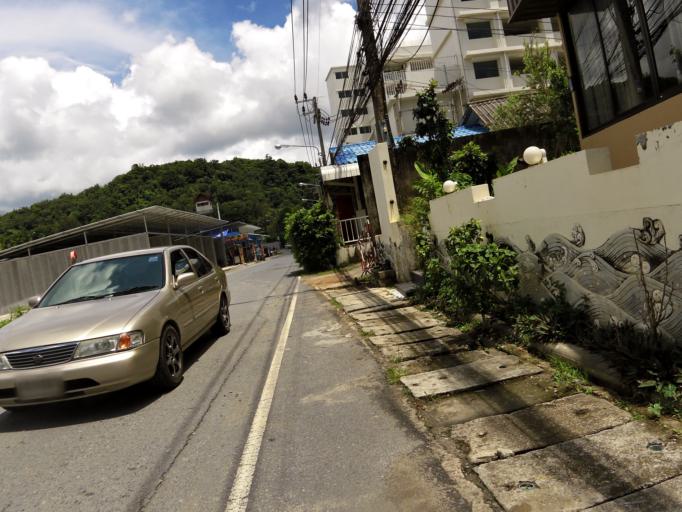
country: TH
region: Phuket
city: Ban Karon
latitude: 7.8539
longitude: 98.2952
